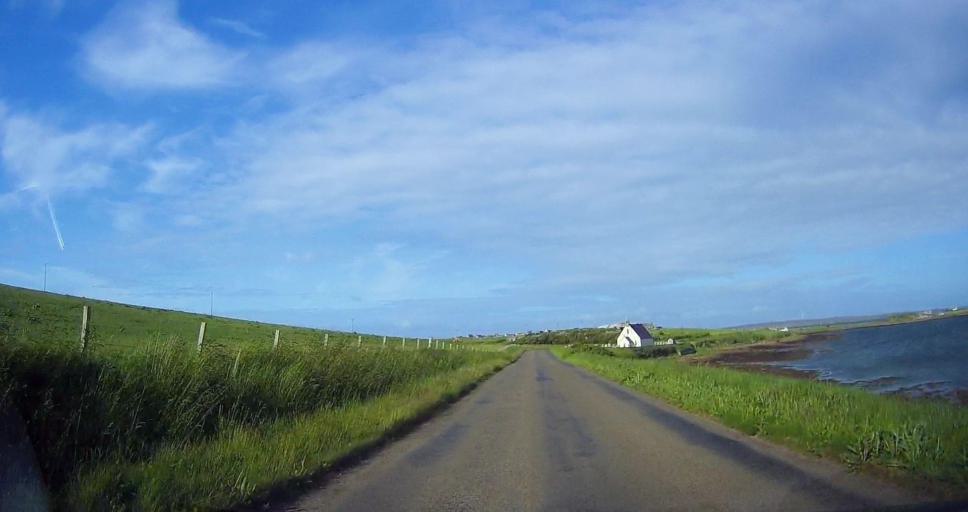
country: GB
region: Scotland
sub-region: Orkney Islands
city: Stromness
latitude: 58.8044
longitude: -3.2206
